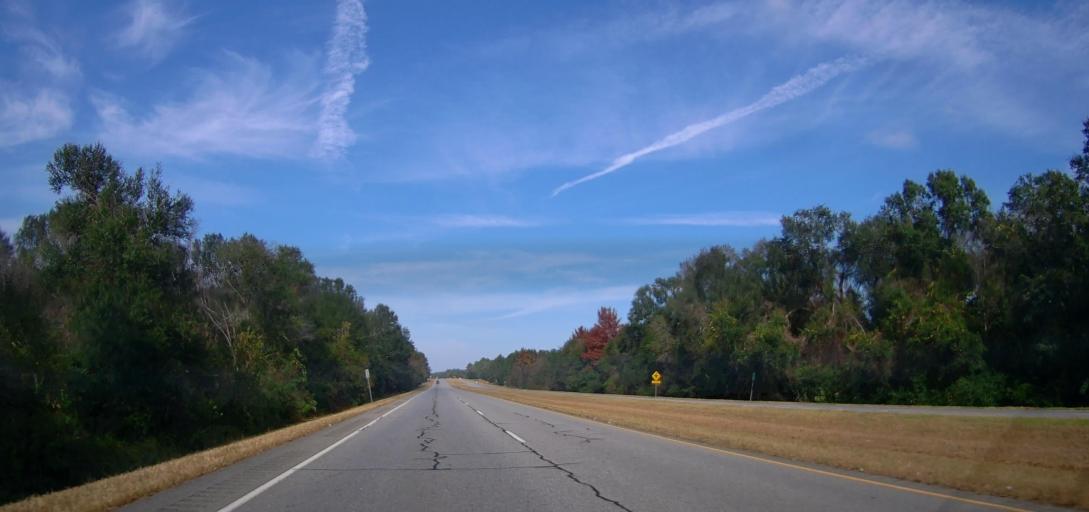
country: US
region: Georgia
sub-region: Mitchell County
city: Camilla
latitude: 31.3060
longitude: -84.1790
